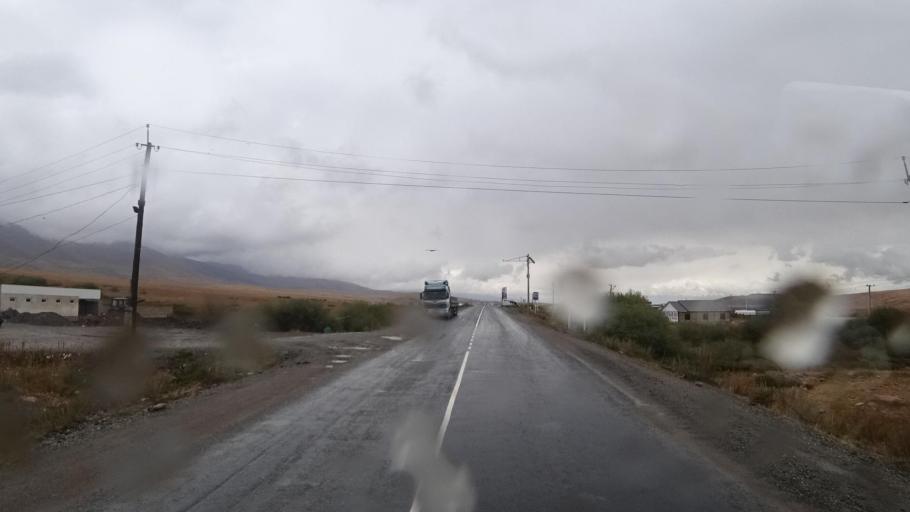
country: KG
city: Sosnovka
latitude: 42.2188
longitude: 73.6936
